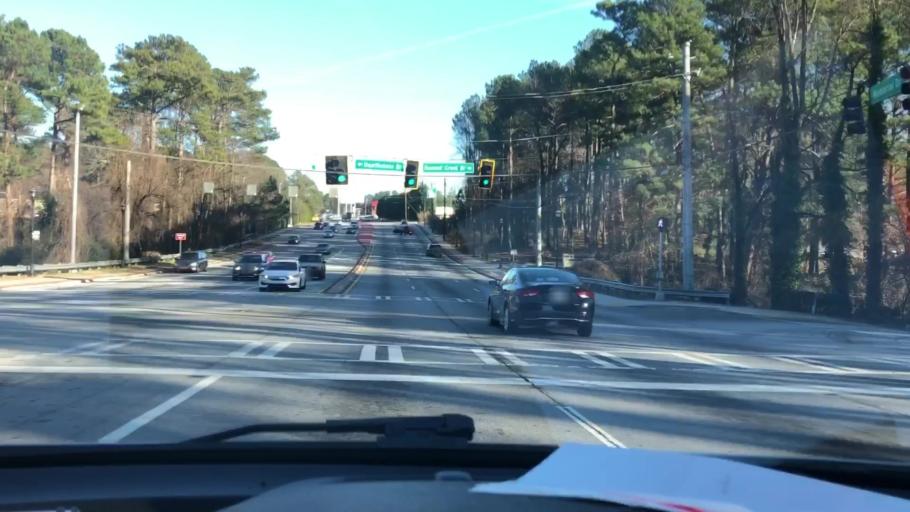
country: US
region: Georgia
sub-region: DeKalb County
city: Stone Mountain
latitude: 33.8006
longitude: -84.2019
